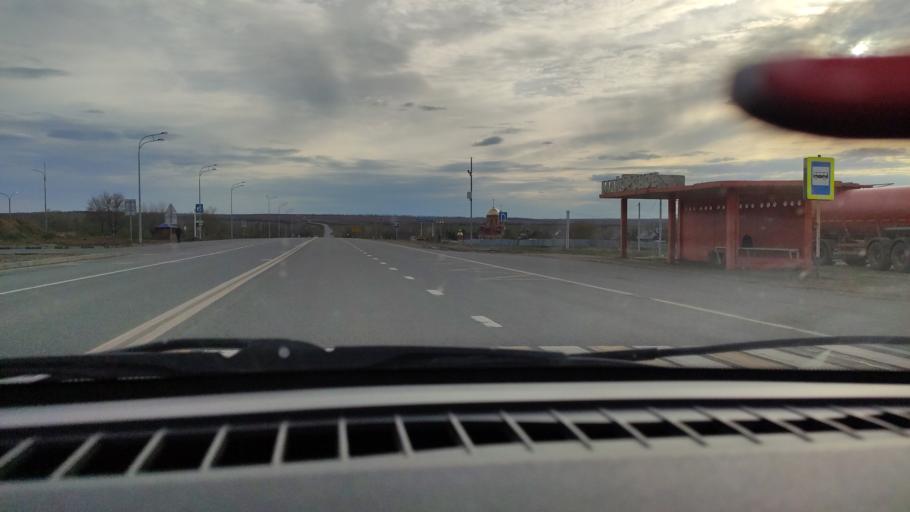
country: RU
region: Orenburg
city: Tatarskaya Kargala
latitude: 52.0271
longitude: 55.2301
